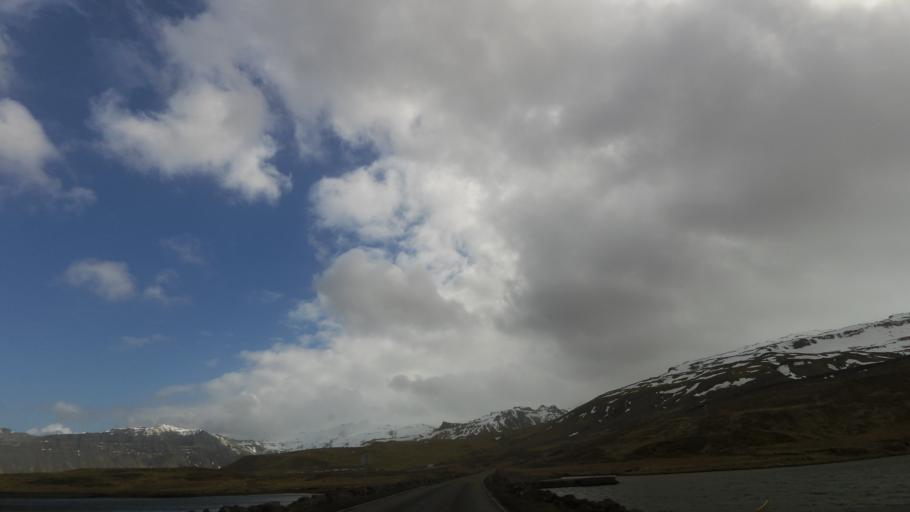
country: IS
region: West
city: Olafsvik
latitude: 64.9269
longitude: -23.3055
